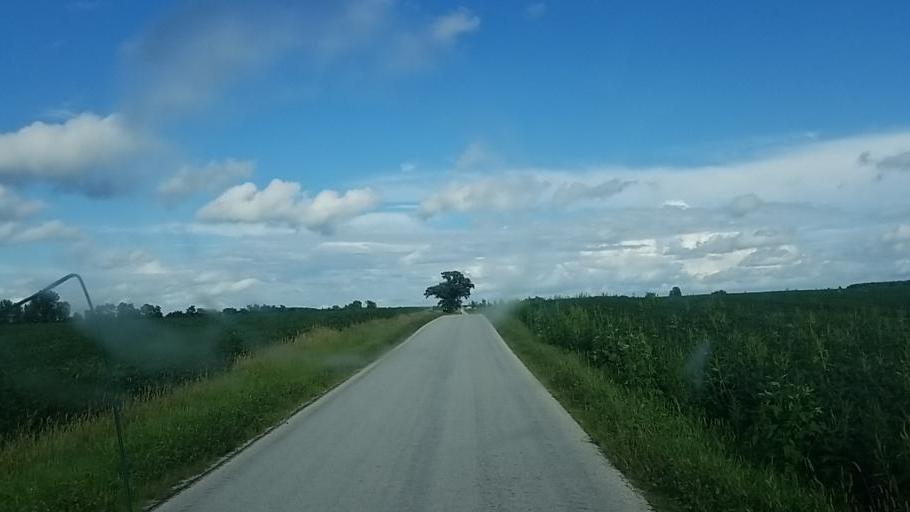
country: US
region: Ohio
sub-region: Hardin County
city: Forest
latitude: 40.7450
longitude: -83.5111
